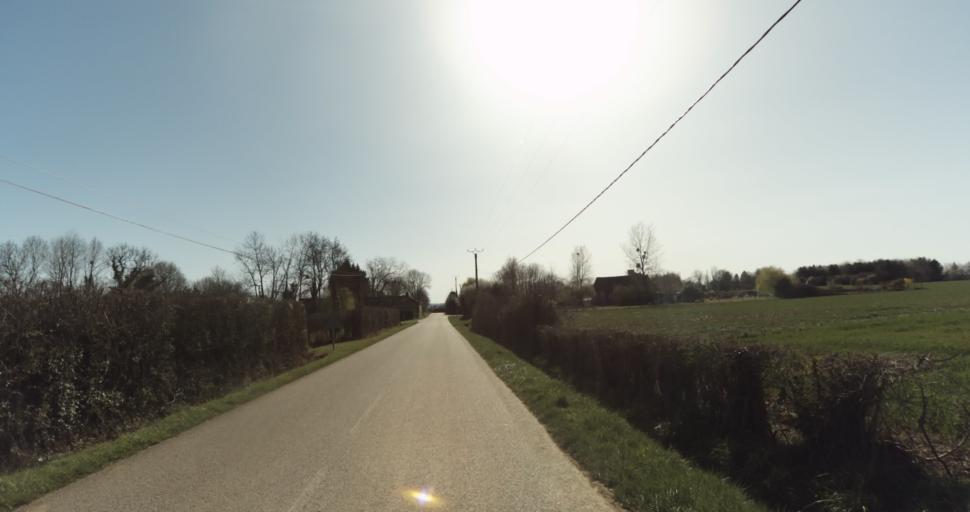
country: FR
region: Lower Normandy
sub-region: Departement de l'Orne
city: Trun
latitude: 48.8915
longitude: 0.0325
